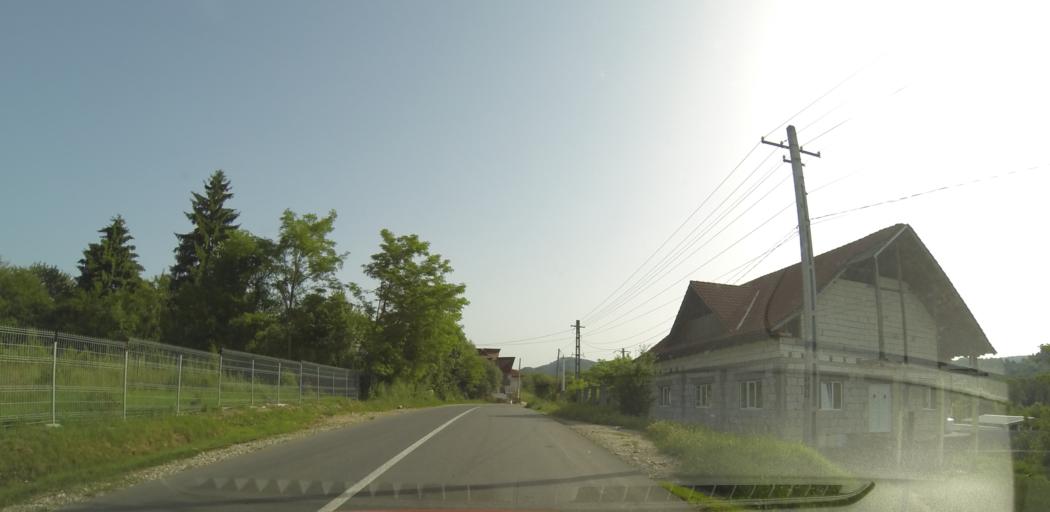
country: RO
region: Valcea
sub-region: Oras Baile Olanesti
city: Olanesti
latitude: 45.1620
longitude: 24.2514
